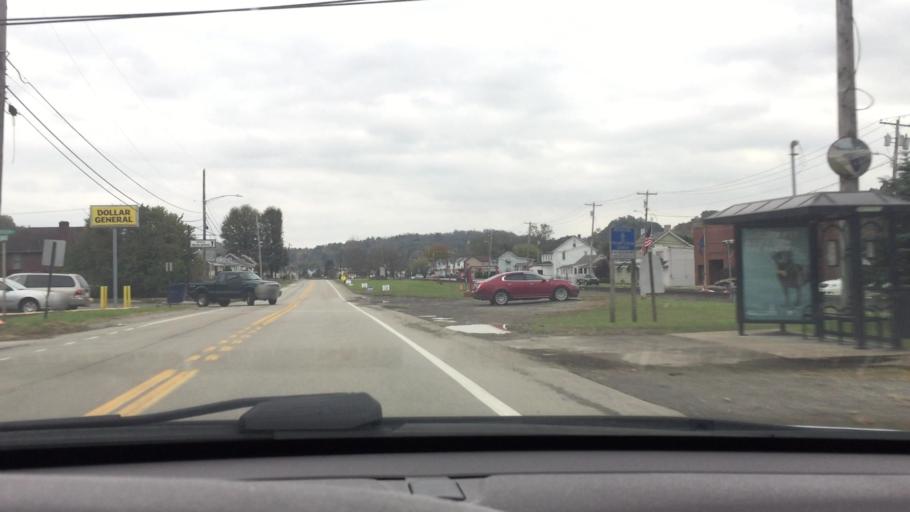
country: US
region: Pennsylvania
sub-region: Washington County
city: California
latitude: 40.0799
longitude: -79.8628
